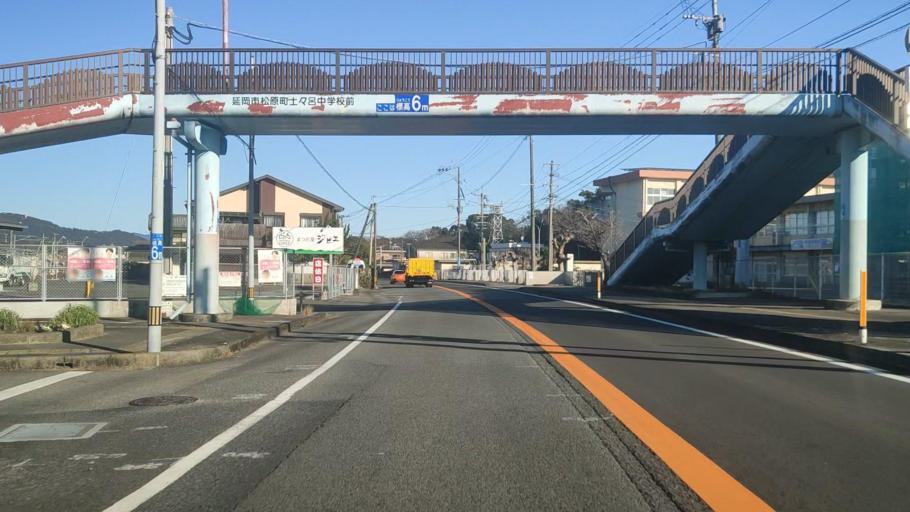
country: JP
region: Miyazaki
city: Nobeoka
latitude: 32.5209
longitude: 131.6835
